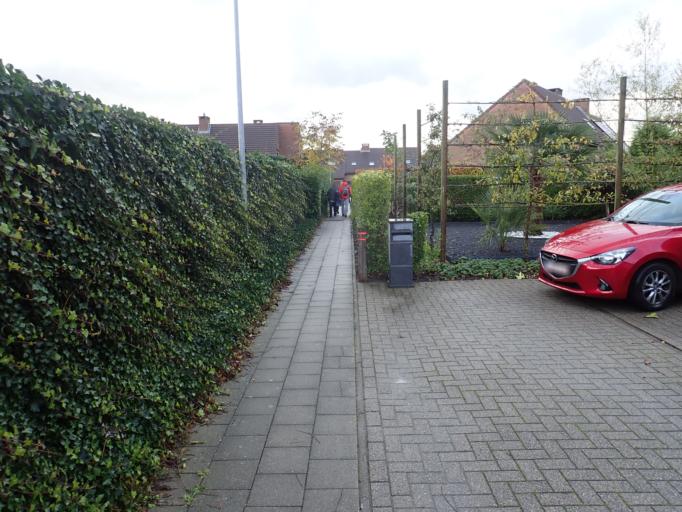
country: BE
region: Flanders
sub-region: Provincie Antwerpen
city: Niel
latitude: 51.0905
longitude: 4.3242
